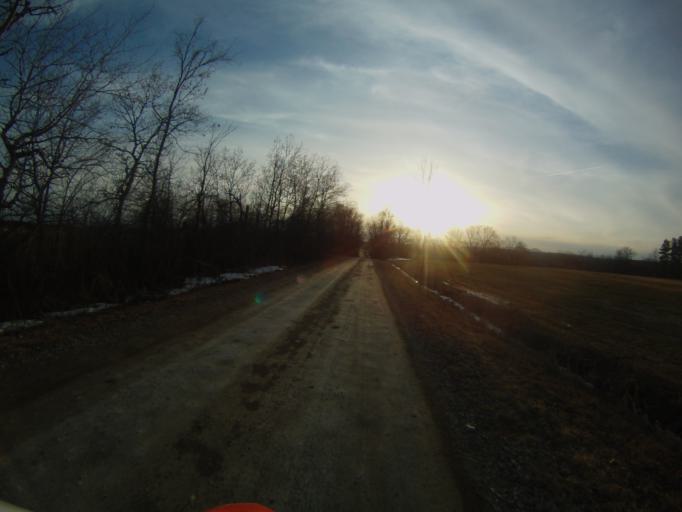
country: US
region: Vermont
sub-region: Addison County
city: Vergennes
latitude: 44.1295
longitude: -73.3218
